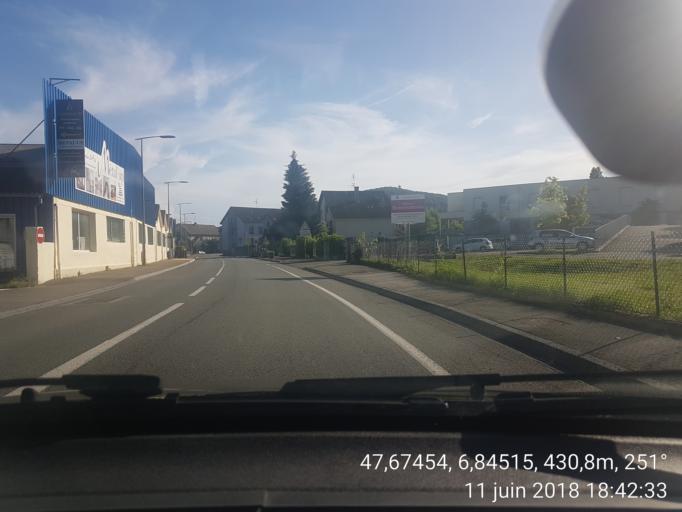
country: FR
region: Franche-Comte
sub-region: Territoire de Belfort
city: Valdoie
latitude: 47.6744
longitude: 6.8451
